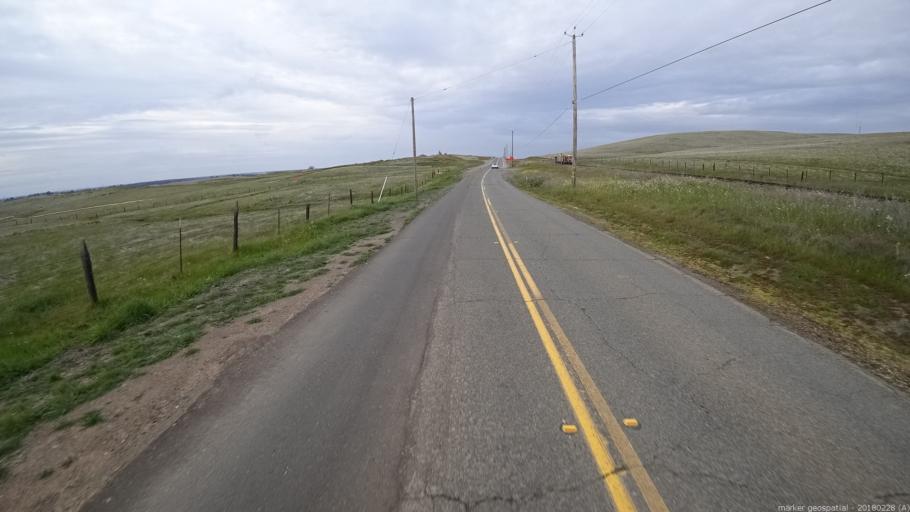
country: US
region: California
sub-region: El Dorado County
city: El Dorado Hills
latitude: 38.6281
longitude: -121.0939
